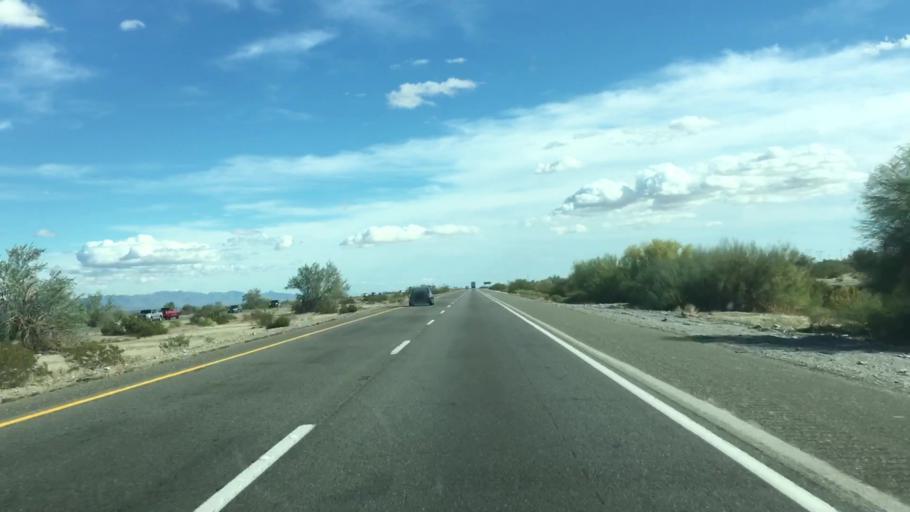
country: US
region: California
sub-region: Imperial County
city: Niland
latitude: 33.6942
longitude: -115.2839
